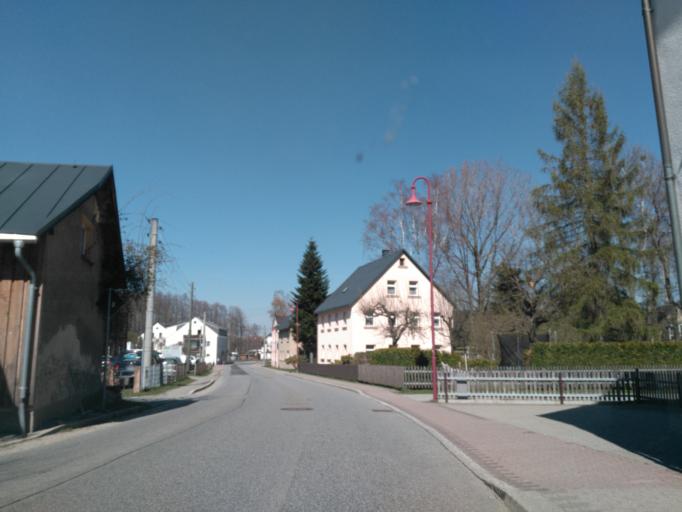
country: DE
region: Saxony
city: Crottendorf
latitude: 50.5088
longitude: 12.9361
